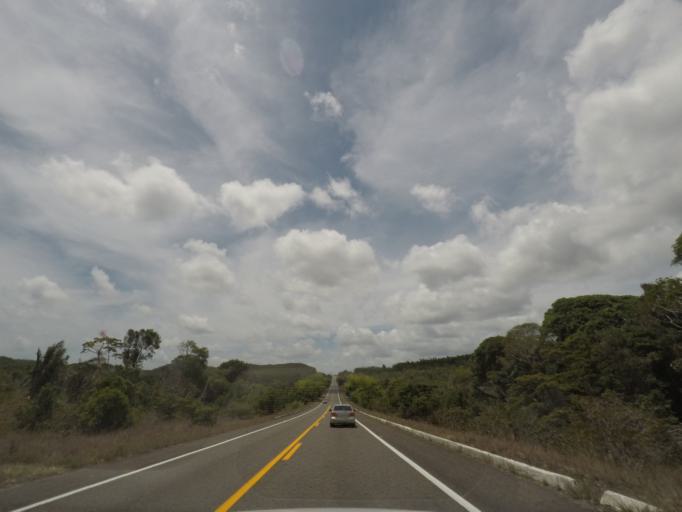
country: BR
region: Sergipe
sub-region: Indiaroba
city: Indiaroba
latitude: -11.6586
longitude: -37.5512
